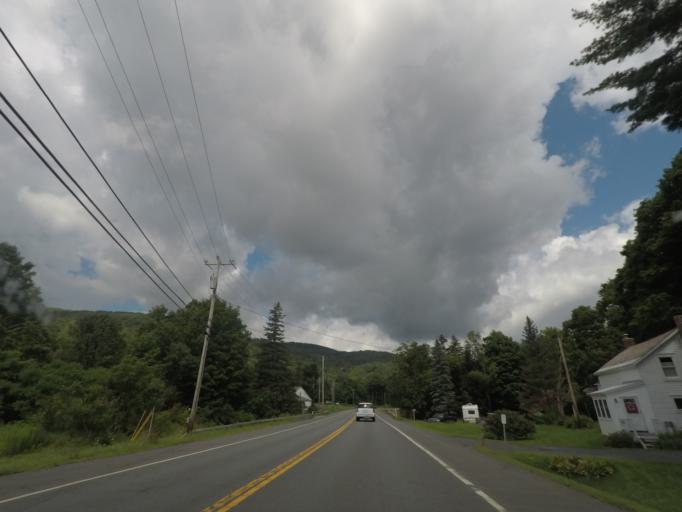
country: US
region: Massachusetts
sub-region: Berkshire County
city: Williamstown
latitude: 42.6600
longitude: -73.3677
